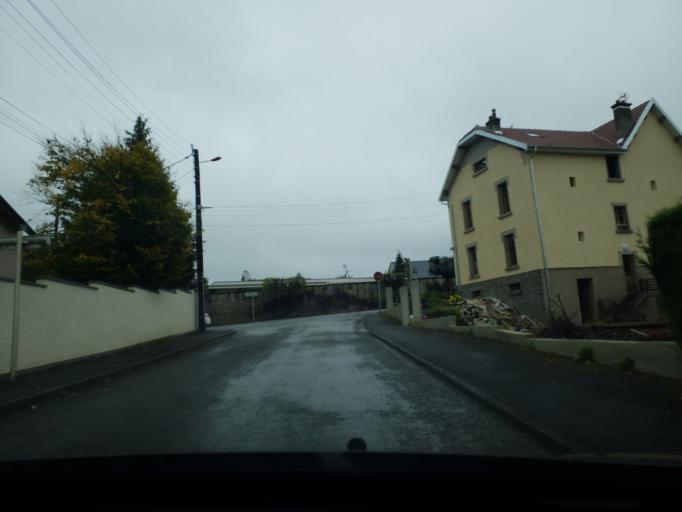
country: FR
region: Franche-Comte
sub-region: Departement de la Haute-Saone
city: Saint-Sauveur
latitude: 47.8161
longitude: 6.3881
